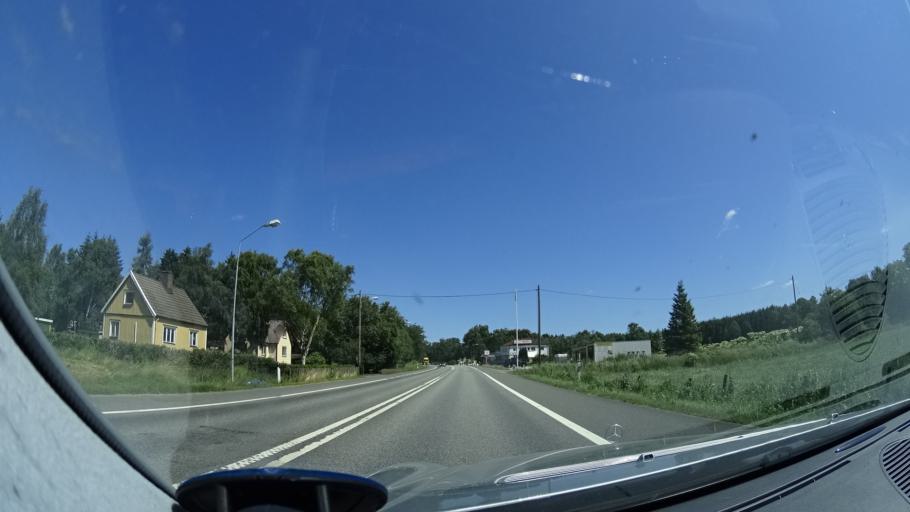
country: SE
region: Skane
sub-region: Hassleholms Kommun
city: Vinslov
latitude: 55.9336
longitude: 13.8327
